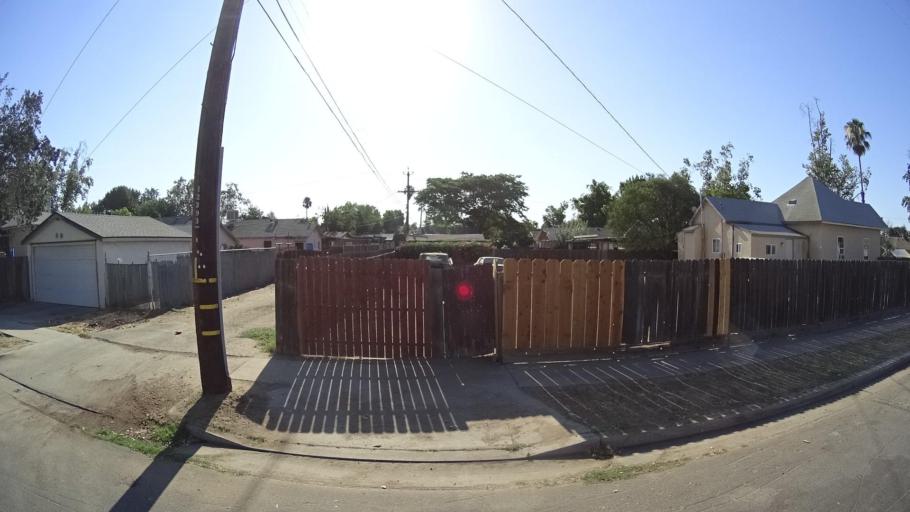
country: US
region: California
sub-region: Fresno County
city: Fresno
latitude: 36.7482
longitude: -119.7677
